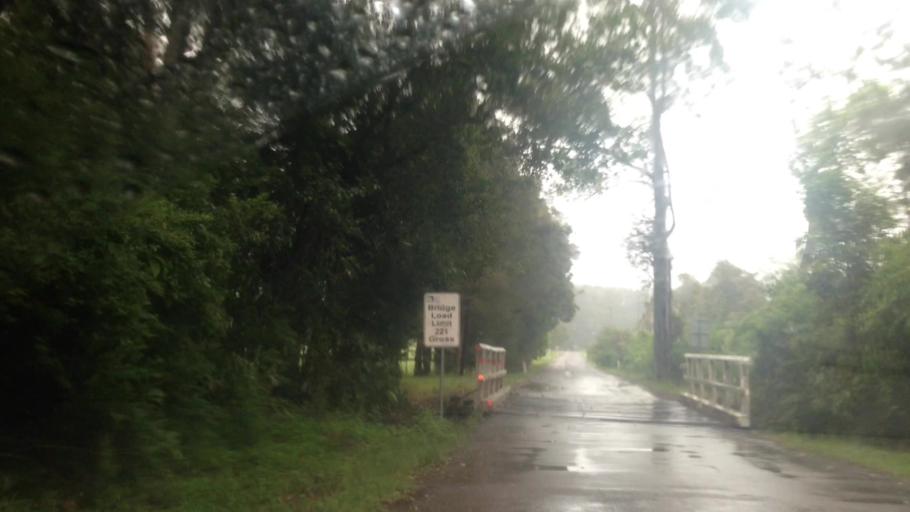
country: AU
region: New South Wales
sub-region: Wyong Shire
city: Little Jilliby
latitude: -33.1903
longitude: 151.3596
